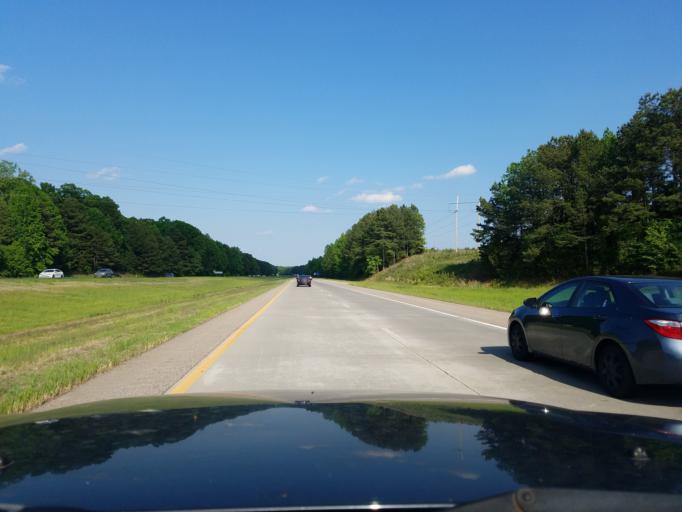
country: US
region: North Carolina
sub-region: Vance County
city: South Henderson
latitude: 36.3205
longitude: -78.4872
